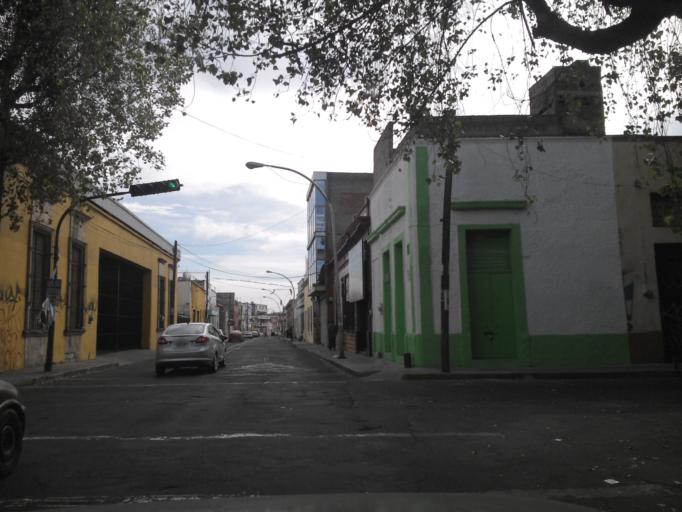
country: MX
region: Jalisco
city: Guadalajara
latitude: 20.6713
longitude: -103.3526
